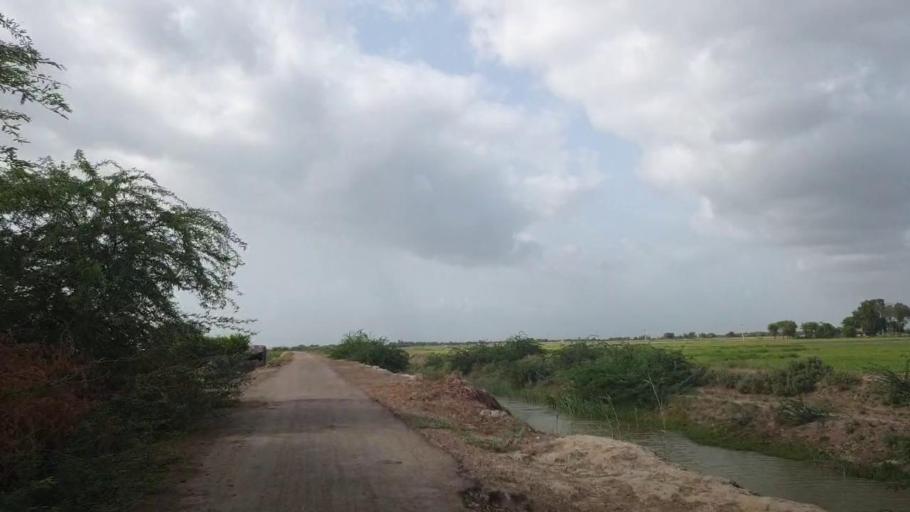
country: PK
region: Sindh
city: Kadhan
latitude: 24.5620
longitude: 69.0639
